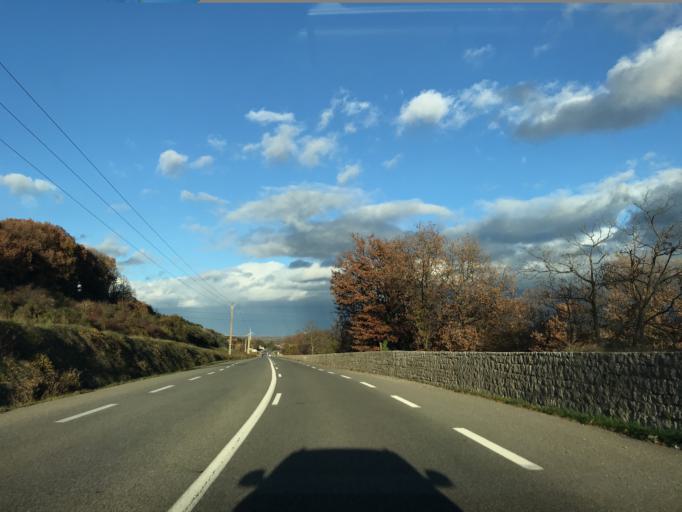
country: FR
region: Rhone-Alpes
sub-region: Departement de l'Ardeche
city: Le Pouzin
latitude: 44.7108
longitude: 4.7253
